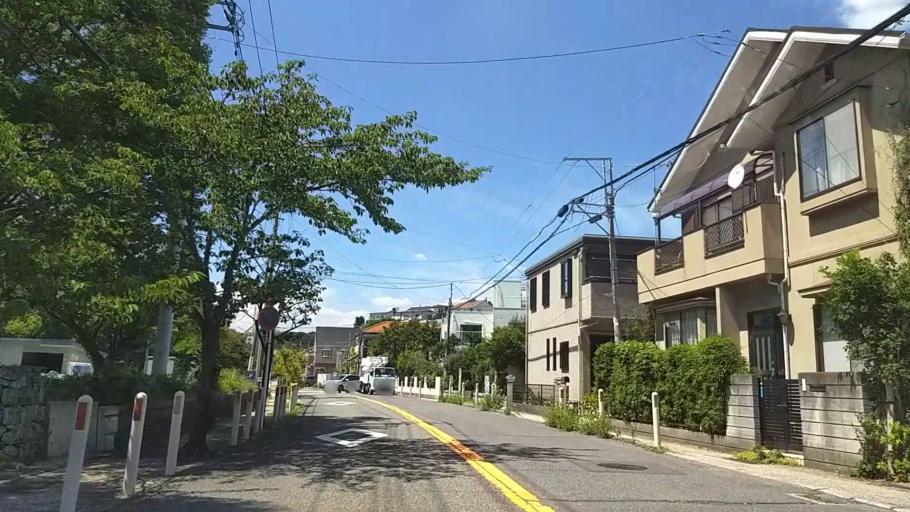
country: JP
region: Kanagawa
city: Zushi
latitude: 35.3009
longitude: 139.5936
